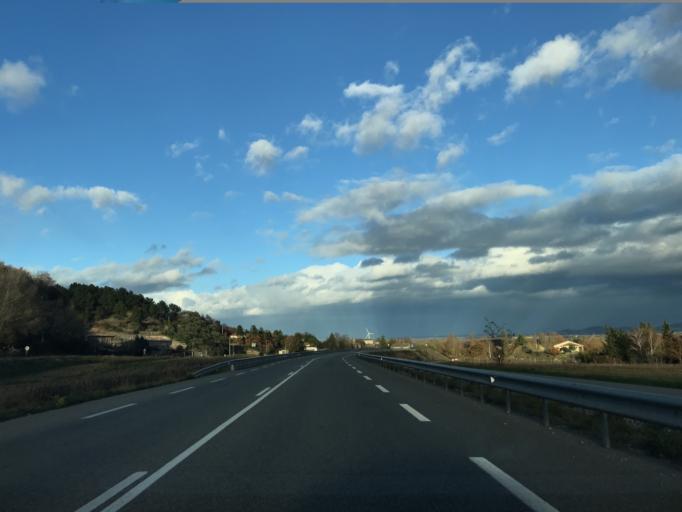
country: FR
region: Rhone-Alpes
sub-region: Departement de l'Ardeche
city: Le Pouzin
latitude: 44.7146
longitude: 4.7288
